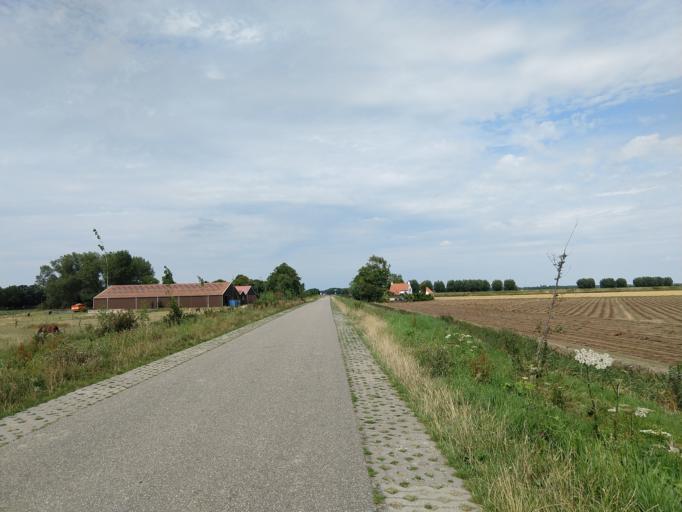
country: NL
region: Zeeland
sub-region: Gemeente Veere
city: Veere
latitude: 51.4897
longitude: 3.6834
